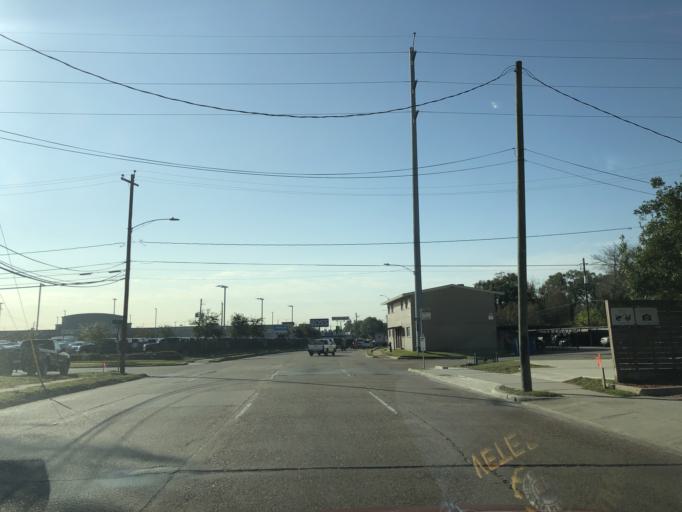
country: US
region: Texas
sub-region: Harris County
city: Houston
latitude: 29.7929
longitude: -95.4116
